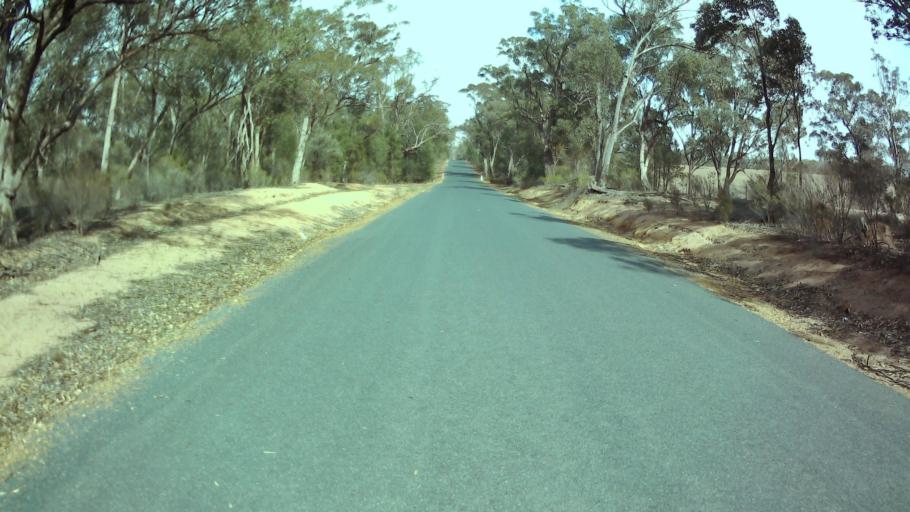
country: AU
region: New South Wales
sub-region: Weddin
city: Grenfell
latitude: -33.8029
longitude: 148.0216
